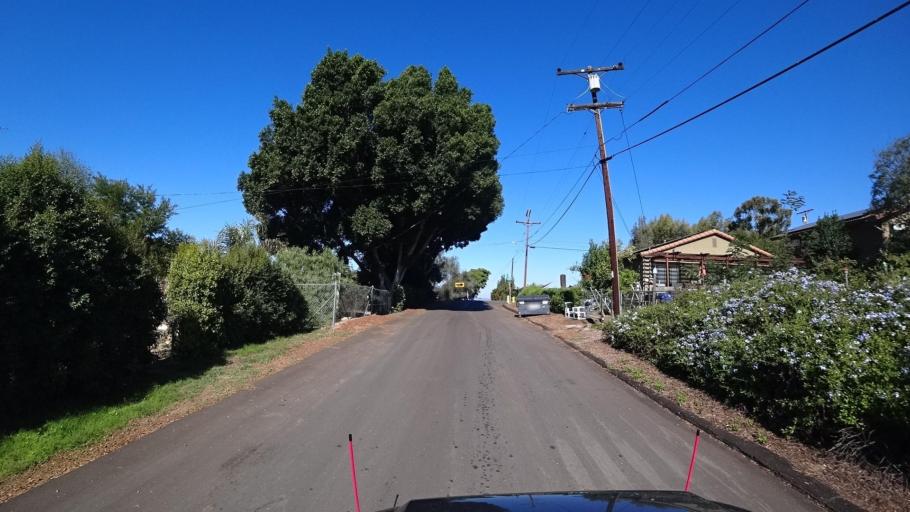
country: US
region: California
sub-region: San Diego County
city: Jamul
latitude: 32.7268
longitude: -116.8684
